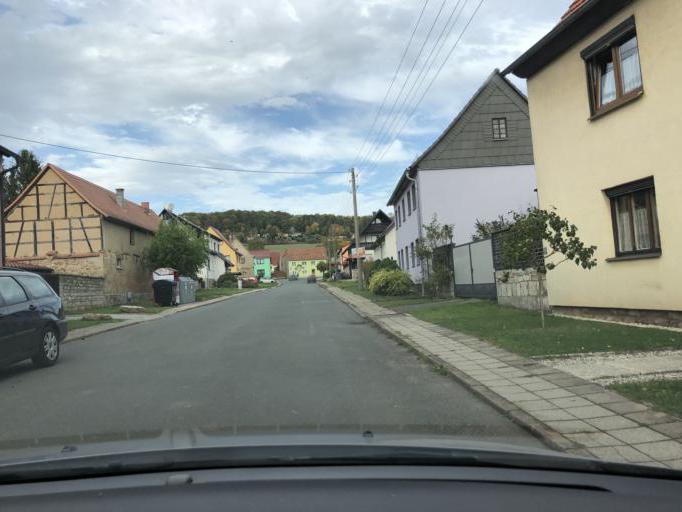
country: DE
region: Thuringia
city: Tonndorf
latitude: 50.8887
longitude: 11.2021
